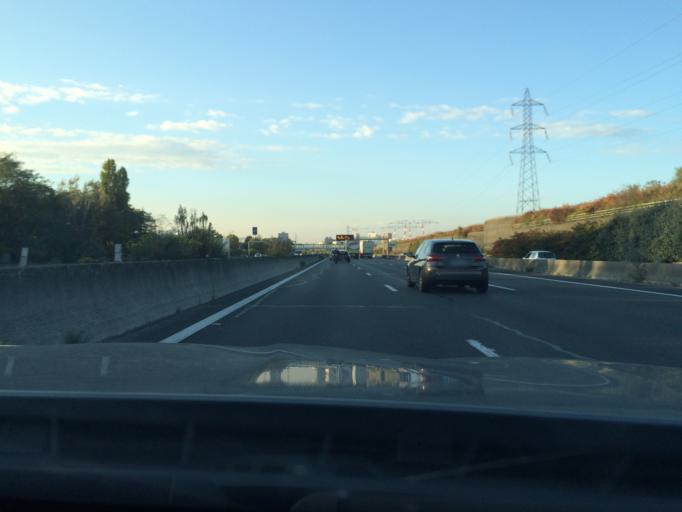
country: FR
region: Ile-de-France
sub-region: Departement de l'Essonne
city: Lisses
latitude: 48.6119
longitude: 2.4319
